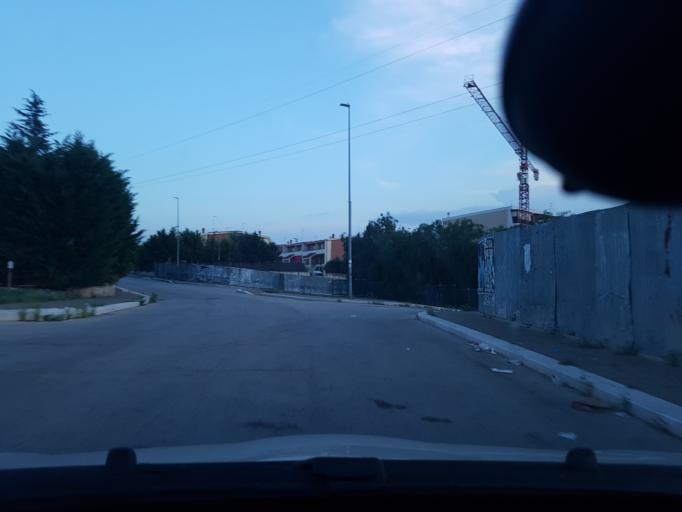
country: IT
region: Apulia
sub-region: Provincia di Foggia
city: Cerignola
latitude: 41.2620
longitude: 15.8780
